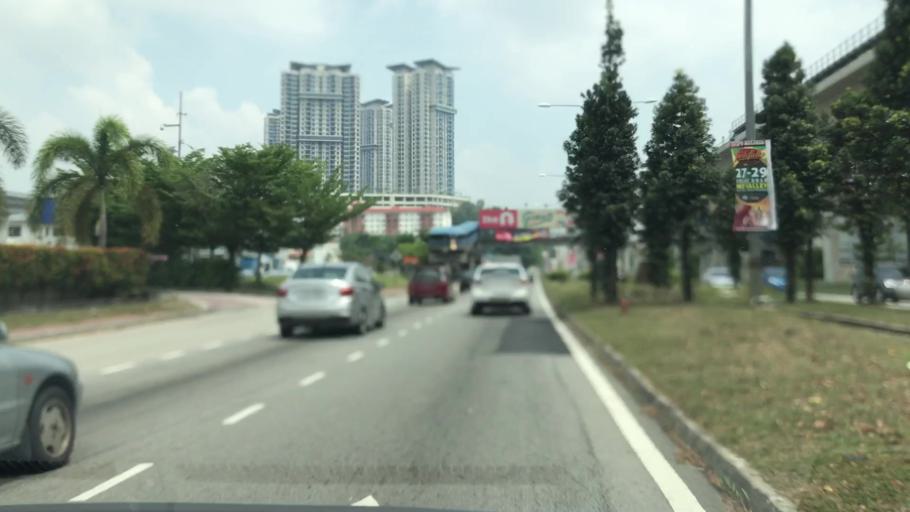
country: MY
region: Selangor
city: Subang Jaya
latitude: 3.0492
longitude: 101.6380
